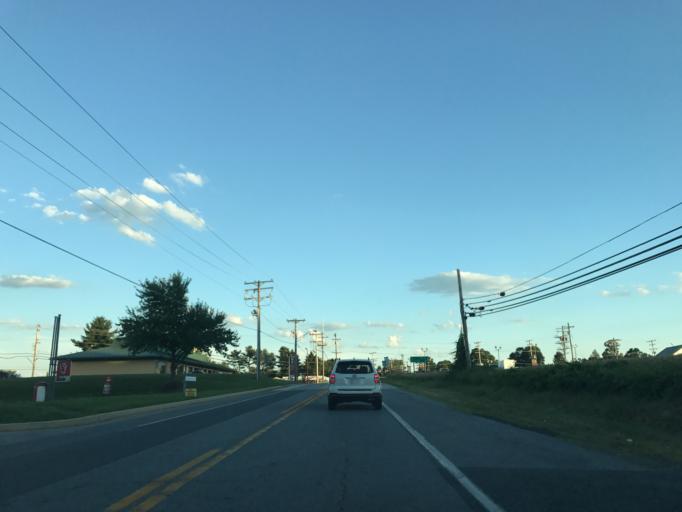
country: US
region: Maryland
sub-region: Harford County
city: Jarrettsville
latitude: 39.6062
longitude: -76.4779
